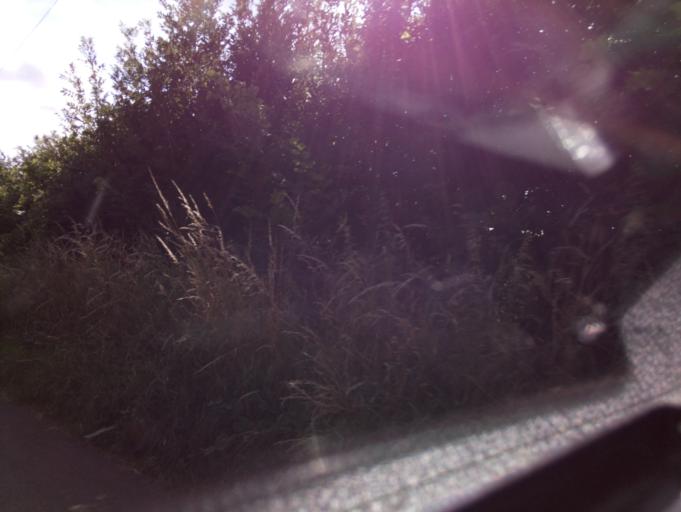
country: GB
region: England
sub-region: Gloucestershire
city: Tetbury
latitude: 51.6670
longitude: -2.1452
